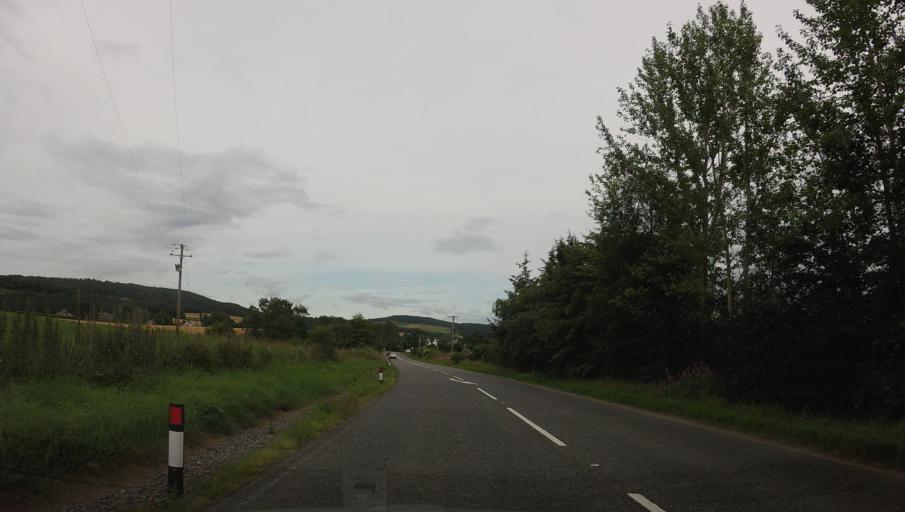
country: GB
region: Scotland
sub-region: Aberdeenshire
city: Torphins
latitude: 57.0873
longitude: -2.6870
